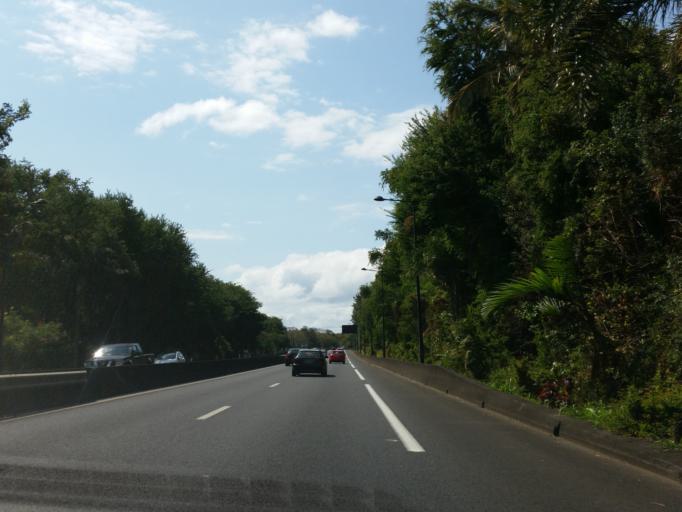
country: RE
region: Reunion
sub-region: Reunion
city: Saint-Denis
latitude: -20.8865
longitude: 55.4931
